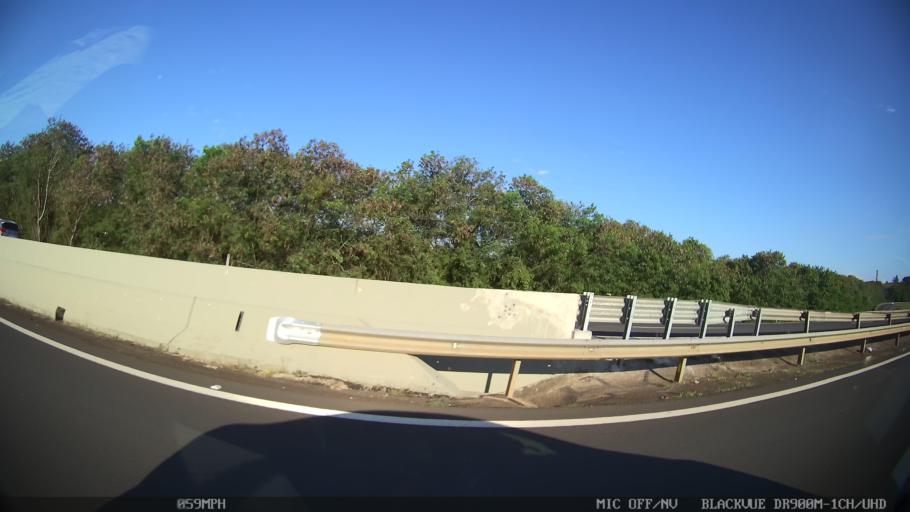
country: BR
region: Sao Paulo
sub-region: Piracicaba
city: Piracicaba
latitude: -22.6928
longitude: -47.6350
